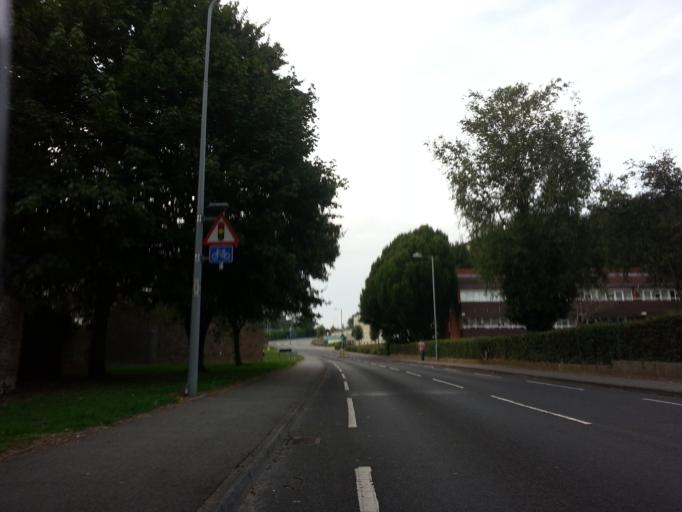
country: GB
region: England
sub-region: Suffolk
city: Ipswich
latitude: 52.0367
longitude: 1.1360
